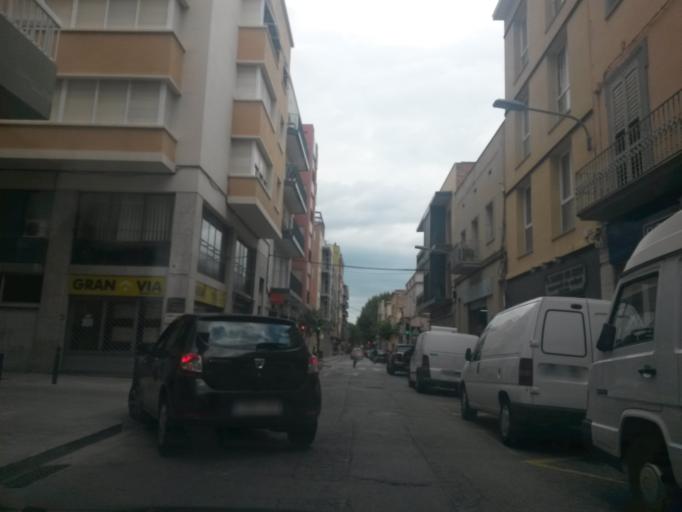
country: ES
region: Catalonia
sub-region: Provincia de Girona
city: Figueres
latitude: 42.2649
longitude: 2.9655
